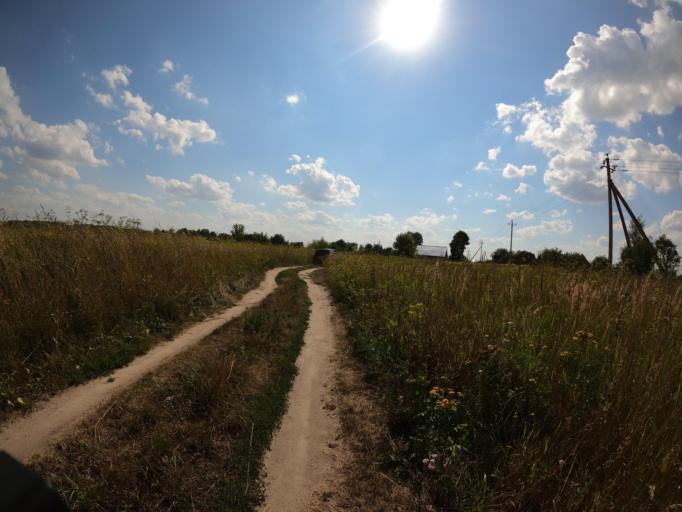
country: RU
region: Moskovskaya
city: Peski
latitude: 55.2303
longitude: 38.7531
